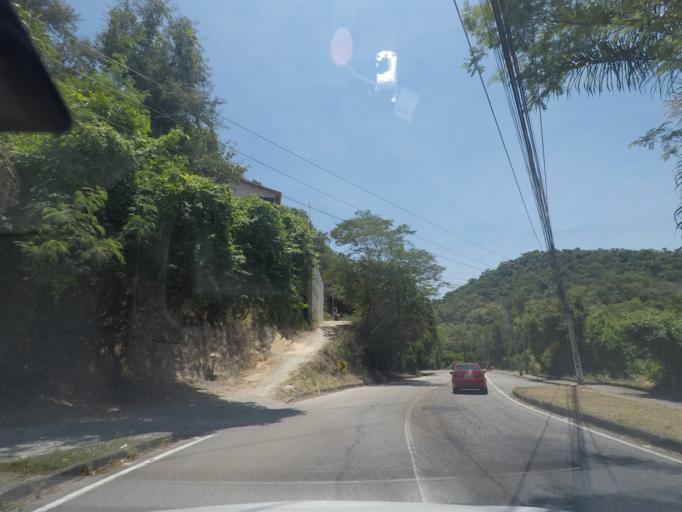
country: BR
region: Rio de Janeiro
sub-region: Niteroi
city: Niteroi
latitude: -22.9204
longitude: -43.0640
